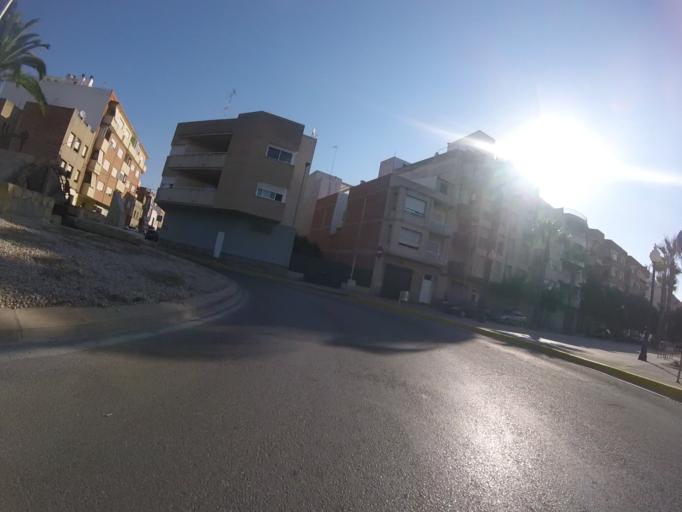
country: ES
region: Valencia
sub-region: Provincia de Castello
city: Benicarlo
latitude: 40.4128
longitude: 0.4225
